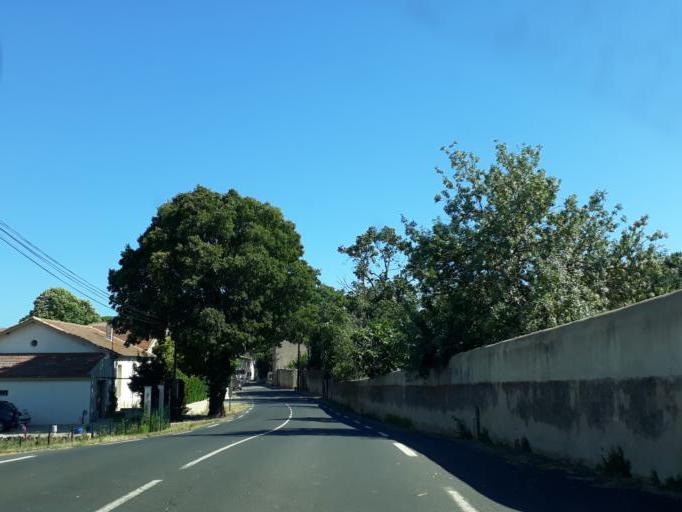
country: FR
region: Languedoc-Roussillon
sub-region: Departement de l'Herault
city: Florensac
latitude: 43.3876
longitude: 3.4623
